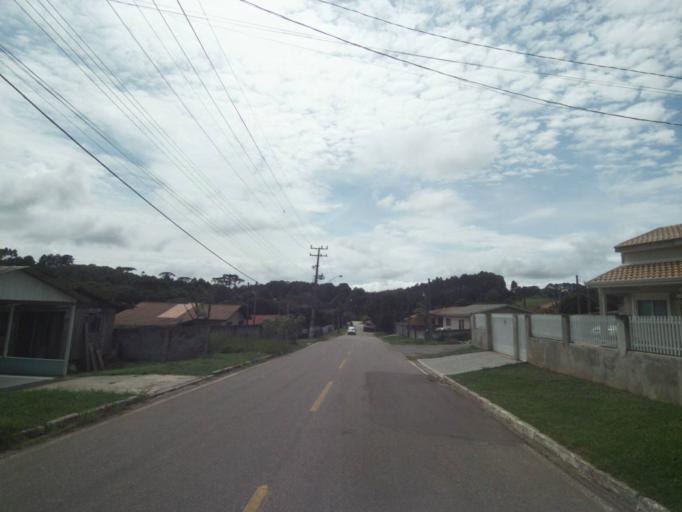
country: BR
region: Parana
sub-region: Campina Grande Do Sul
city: Campina Grande do Sul
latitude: -25.3080
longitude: -49.0506
